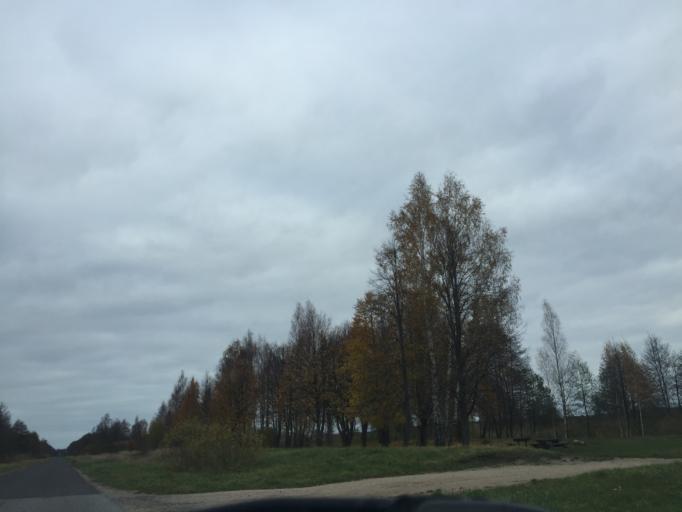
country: LV
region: Liepaja
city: Vec-Liepaja
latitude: 56.5559
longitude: 21.0633
